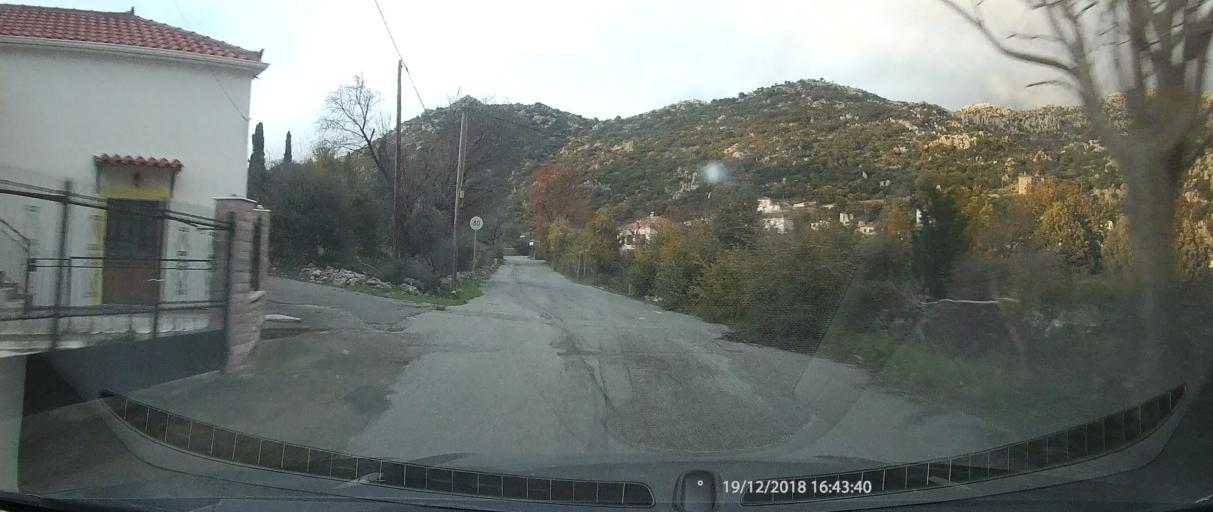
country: GR
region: Peloponnese
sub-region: Nomos Lakonias
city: Sykea
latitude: 36.9144
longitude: 22.9968
